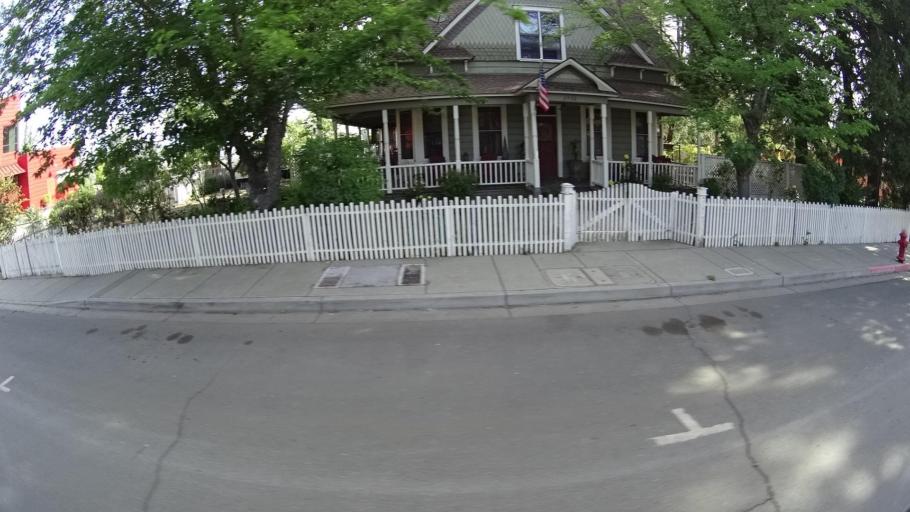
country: US
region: California
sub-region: Lake County
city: Kelseyville
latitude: 38.9783
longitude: -122.8411
